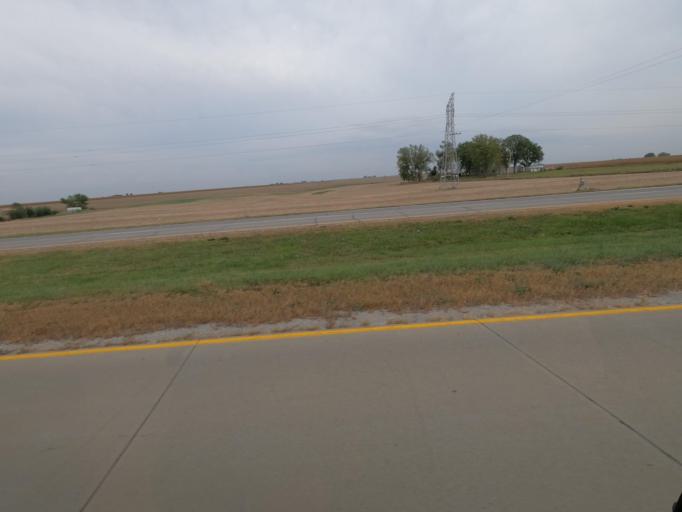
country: US
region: Iowa
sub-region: Jasper County
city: Monroe
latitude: 41.4494
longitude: -93.0239
